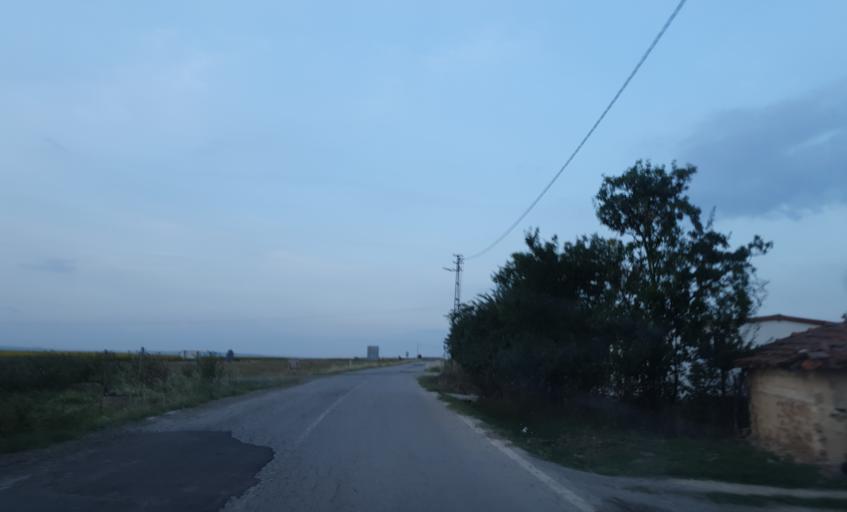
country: TR
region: Tekirdag
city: Beyazkoy
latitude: 41.4142
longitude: 27.6578
